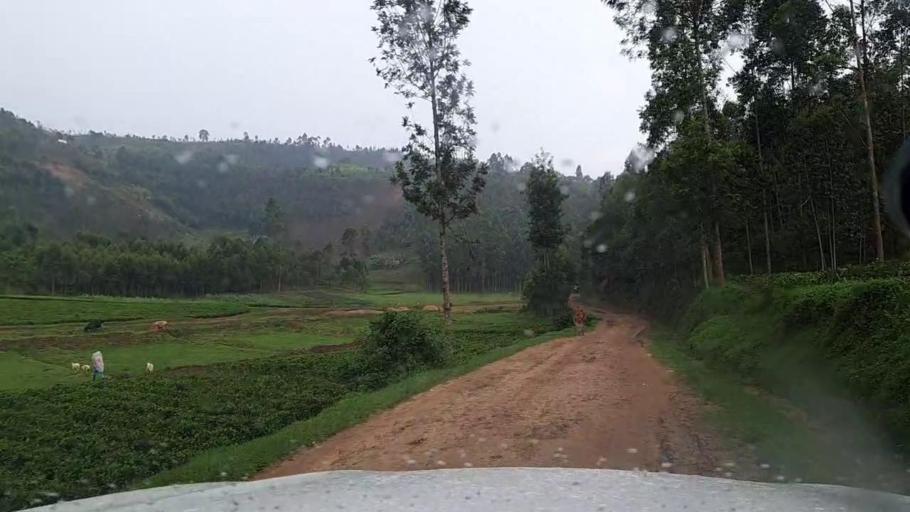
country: RW
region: Northern Province
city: Byumba
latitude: -1.6522
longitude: 29.9265
